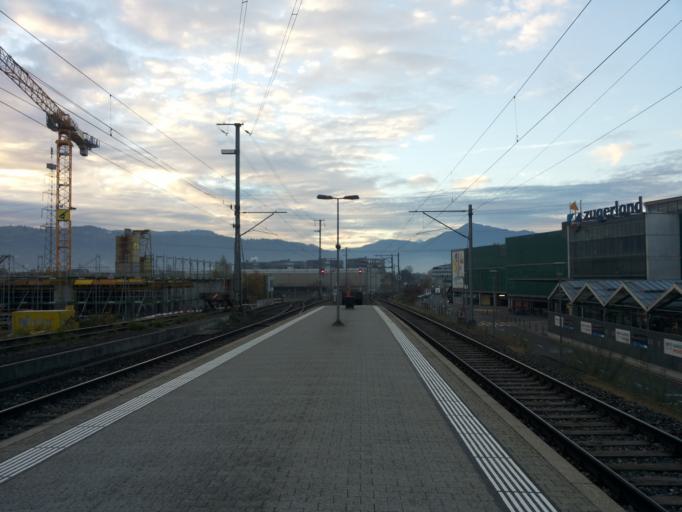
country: CH
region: Zug
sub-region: Zug
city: Steinhausen
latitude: 47.1930
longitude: 8.4787
